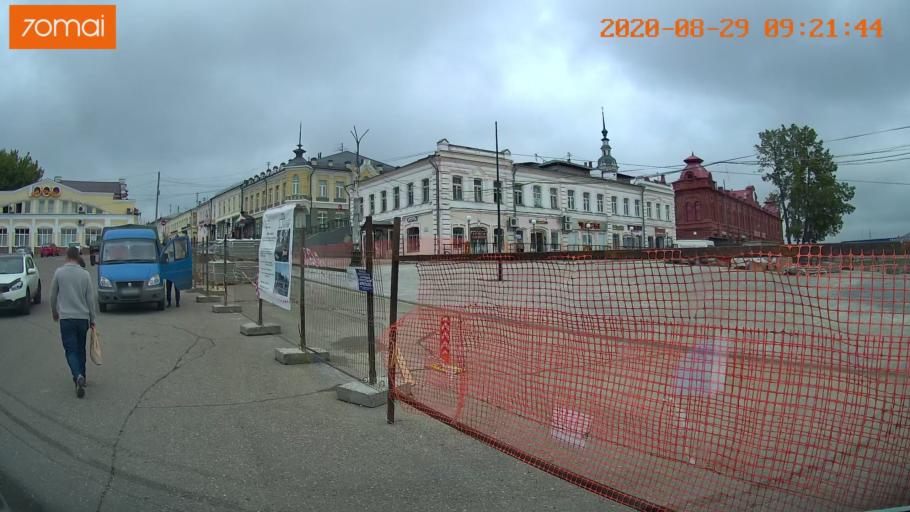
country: RU
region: Ivanovo
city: Kineshma
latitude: 57.4428
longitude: 42.1694
